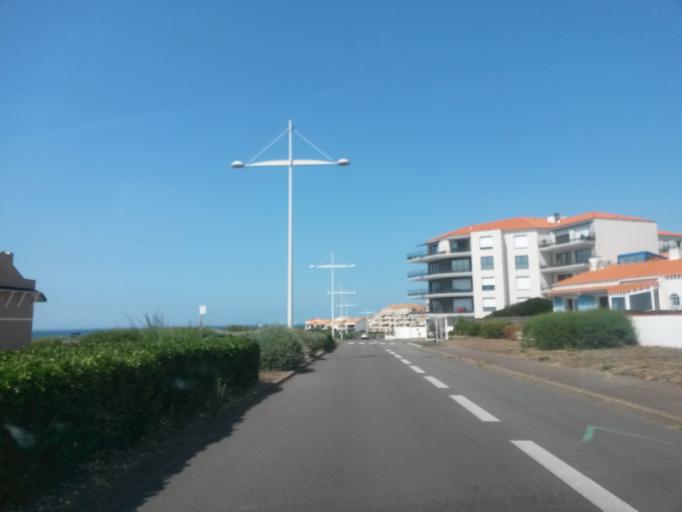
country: FR
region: Pays de la Loire
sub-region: Departement de la Vendee
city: Les Sables-d'Olonne
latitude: 46.4907
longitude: -1.8043
